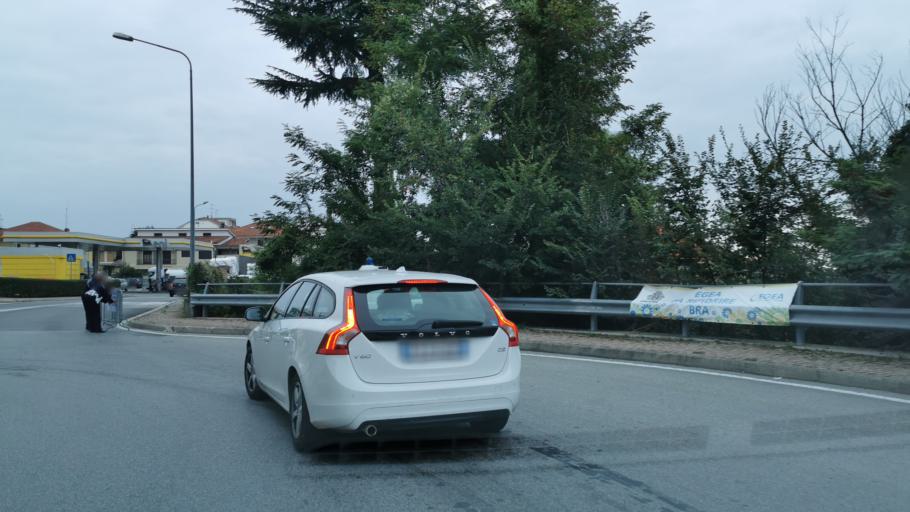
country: IT
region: Piedmont
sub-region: Provincia di Cuneo
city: Bra
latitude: 44.6842
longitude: 7.8500
